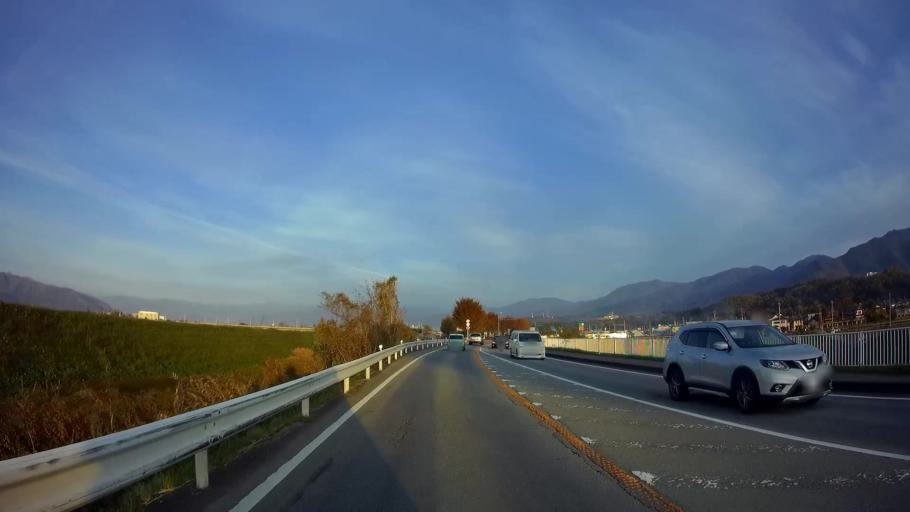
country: JP
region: Yamanashi
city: Kofu-shi
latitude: 35.5960
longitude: 138.5686
